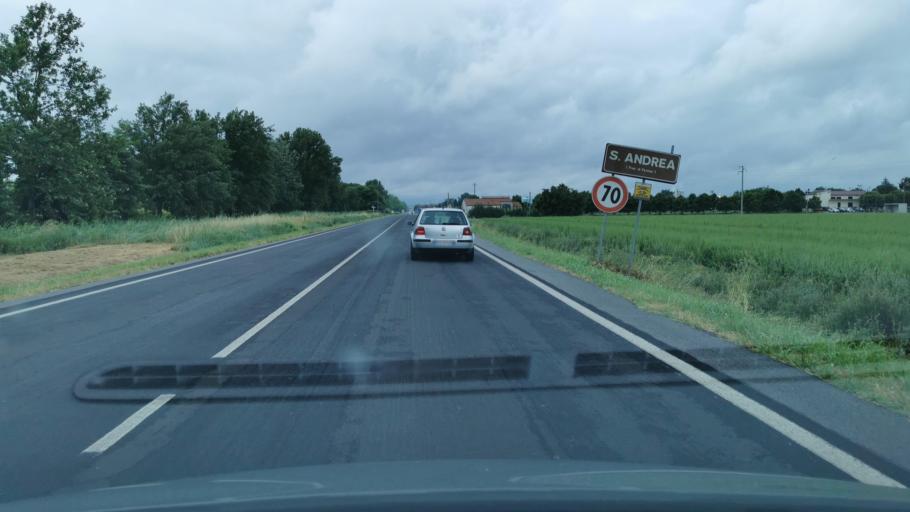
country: IT
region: Emilia-Romagna
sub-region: Provincia di Ravenna
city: Granarolo
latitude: 44.3380
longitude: 11.9178
